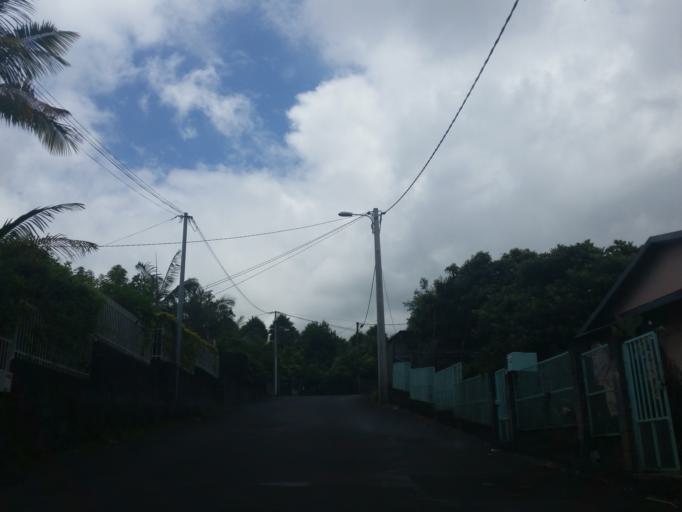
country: RE
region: Reunion
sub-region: Reunion
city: L'Entre-Deux
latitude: -21.2558
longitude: 55.4928
